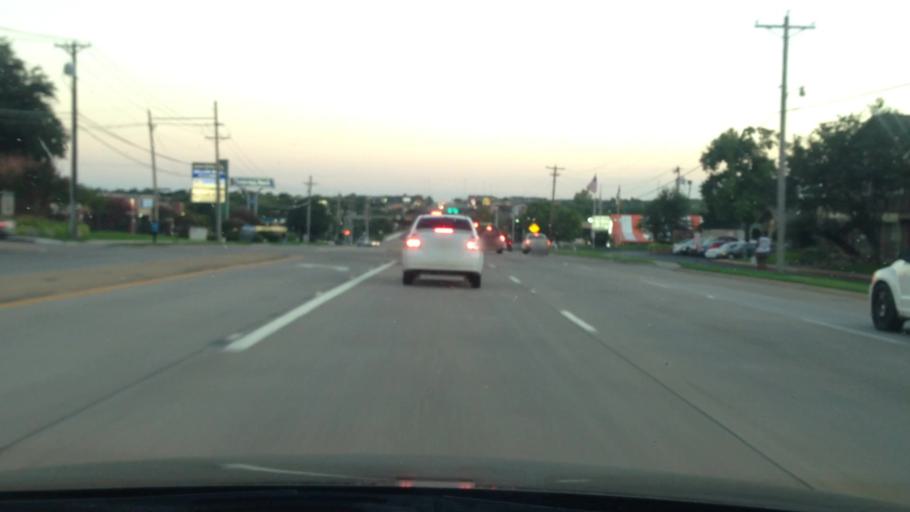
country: US
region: Texas
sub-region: Denton County
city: Lewisville
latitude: 33.0212
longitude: -96.9930
